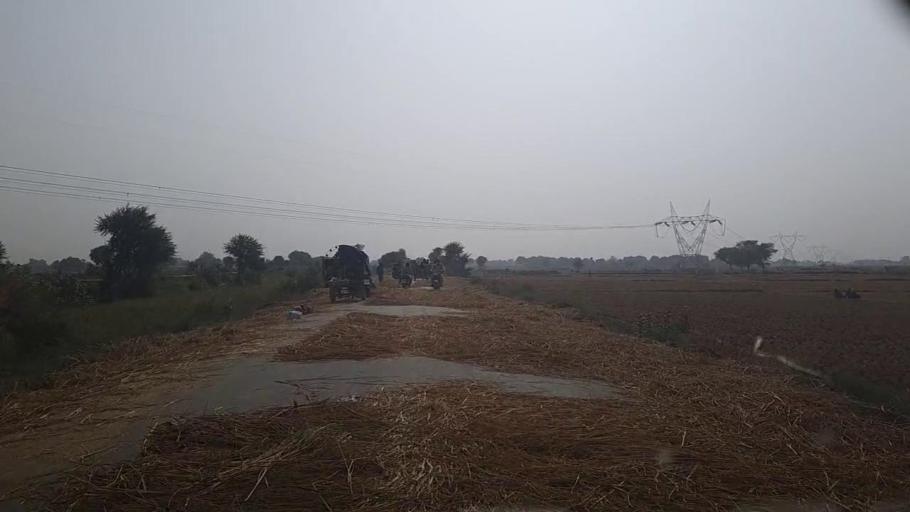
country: PK
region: Sindh
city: Kashmor
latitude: 28.4200
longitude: 69.5703
